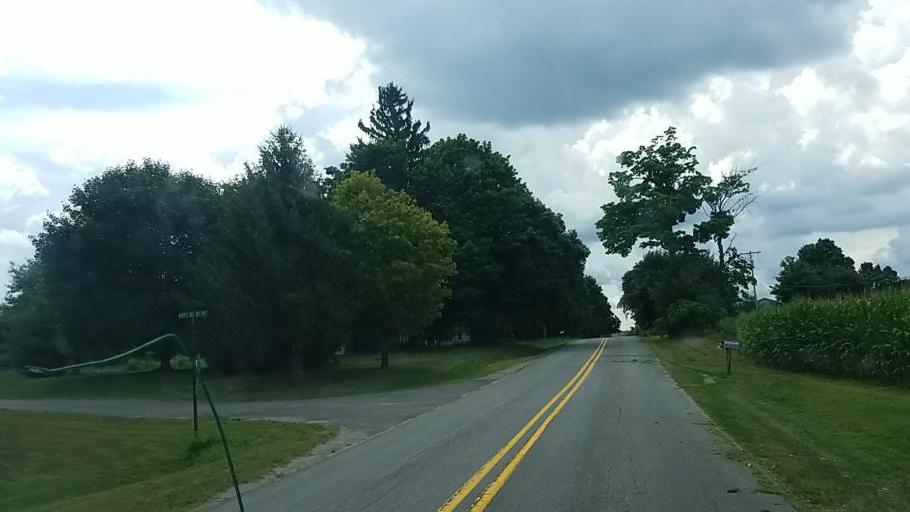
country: US
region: Michigan
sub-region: Kent County
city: Walker
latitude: 43.0527
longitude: -85.7437
